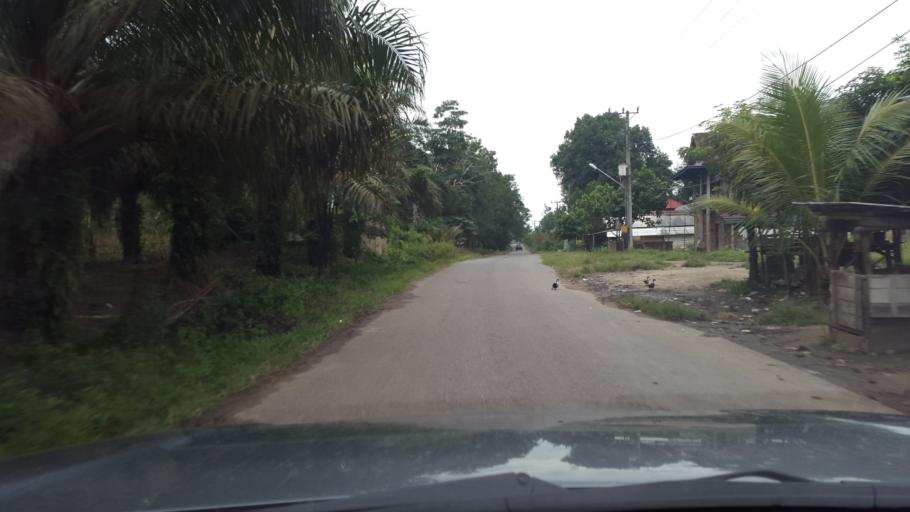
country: ID
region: South Sumatra
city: Gunungmenang
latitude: -3.2687
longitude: 104.0543
